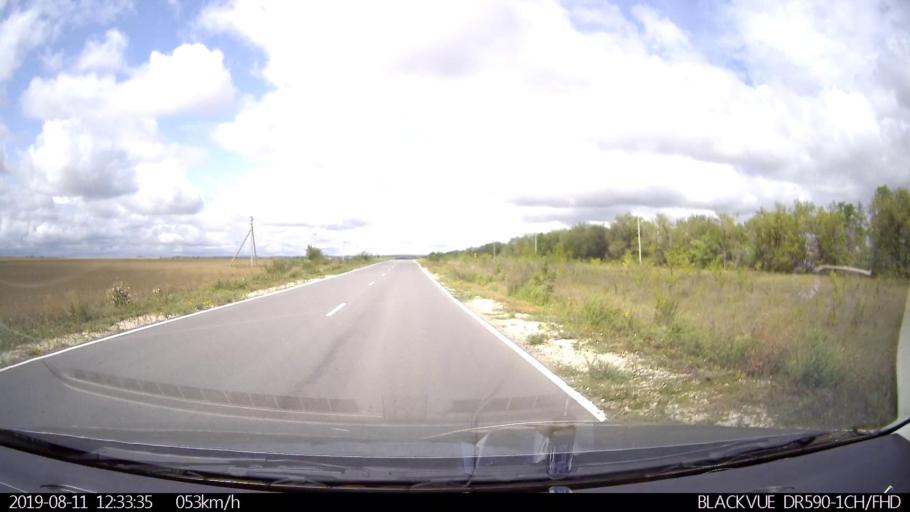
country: RU
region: Ulyanovsk
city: Ignatovka
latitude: 53.8106
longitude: 47.8539
